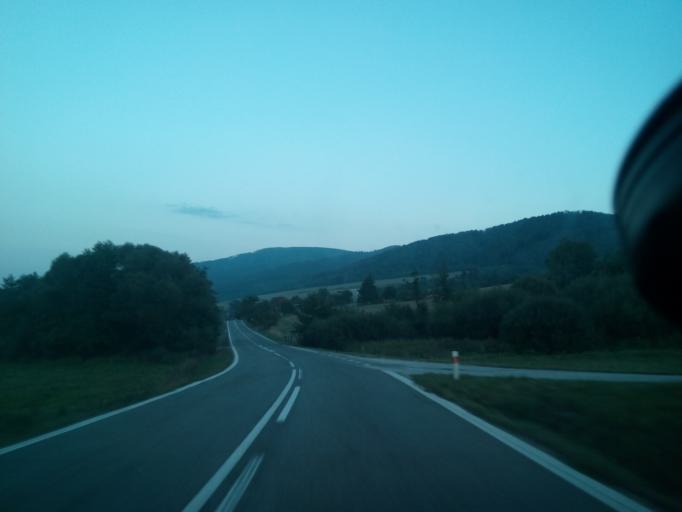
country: SK
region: Kosicky
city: Dobsina
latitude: 48.7168
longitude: 20.4242
